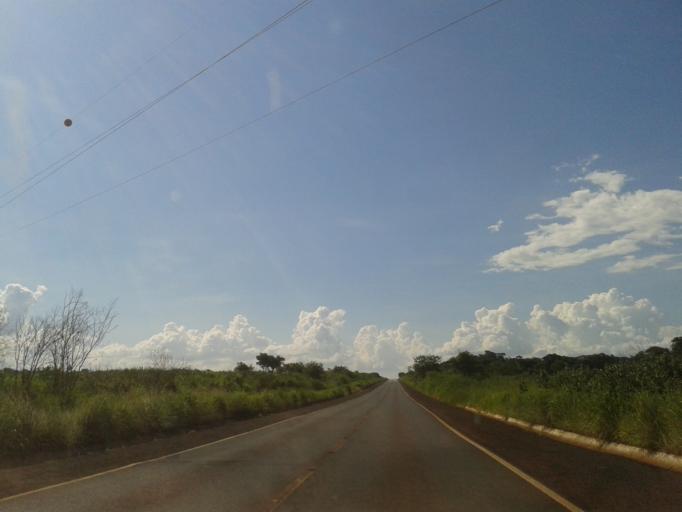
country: BR
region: Minas Gerais
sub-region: Santa Vitoria
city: Santa Vitoria
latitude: -19.0546
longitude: -50.3949
